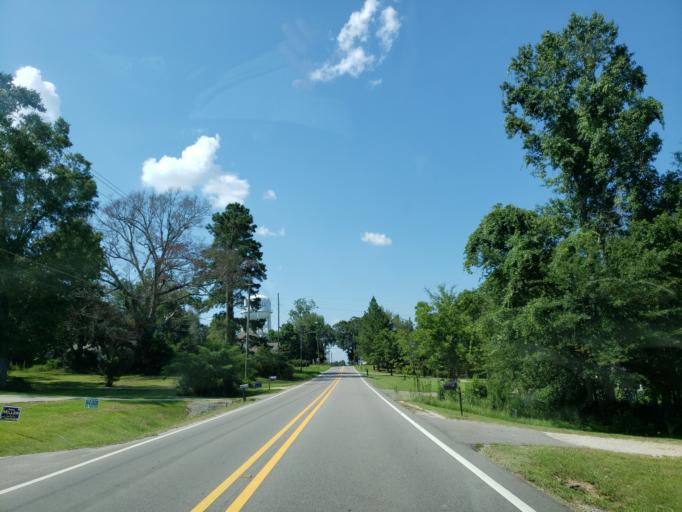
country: US
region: Mississippi
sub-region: Lamar County
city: Sumrall
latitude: 31.4110
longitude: -89.5458
